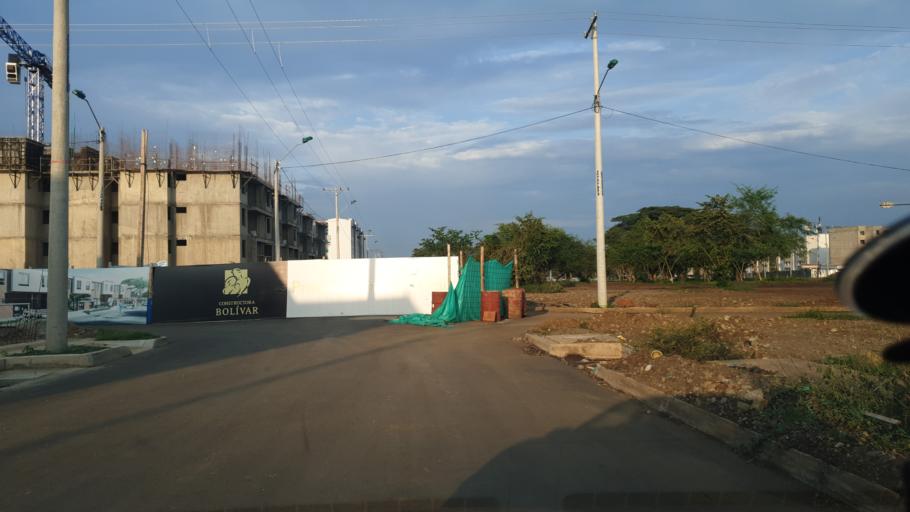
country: CO
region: Valle del Cauca
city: Jamundi
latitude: 3.3459
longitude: -76.5183
